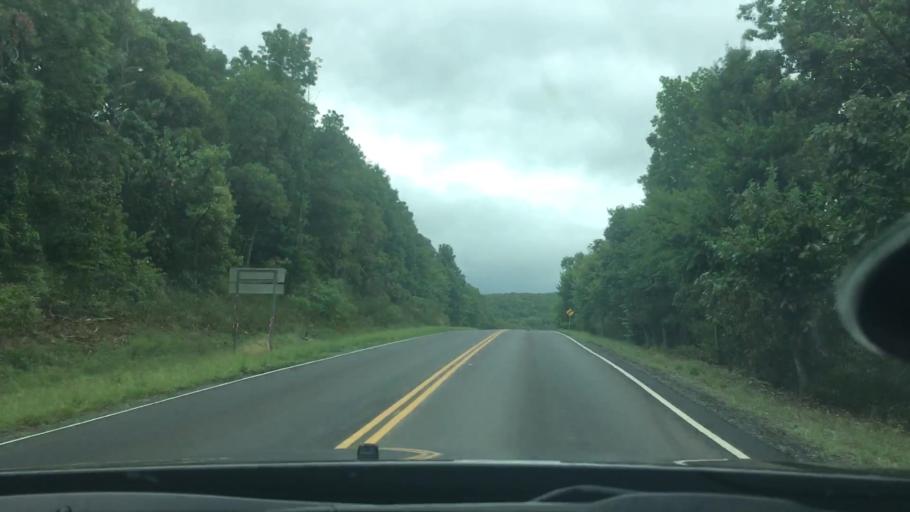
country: US
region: Oklahoma
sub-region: Sequoyah County
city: Vian
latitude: 35.6708
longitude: -94.9336
